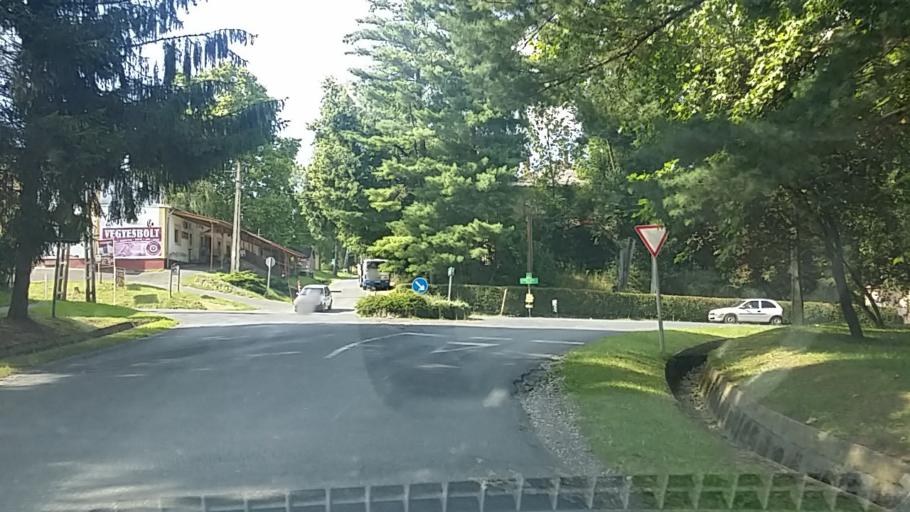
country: HU
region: Zala
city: Becsehely
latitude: 46.5264
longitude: 16.7277
